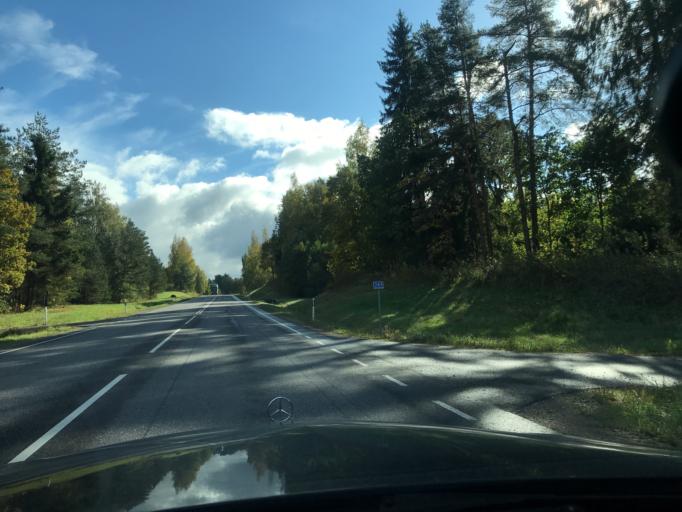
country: EE
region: Vorumaa
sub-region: Voru linn
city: Voru
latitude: 57.8016
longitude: 27.0871
